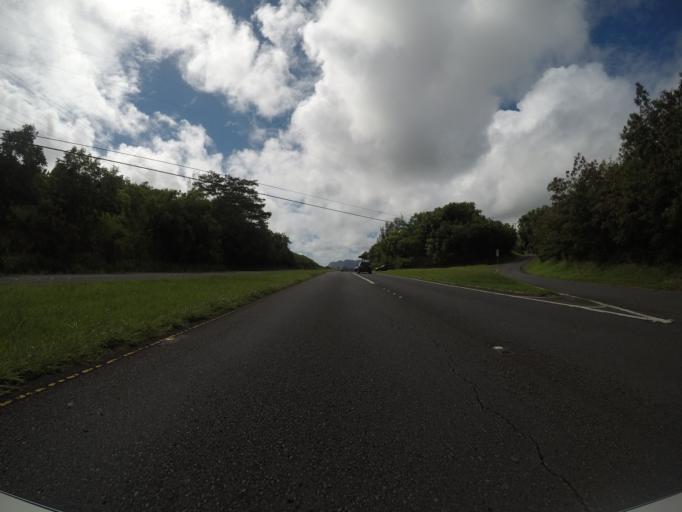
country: US
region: Hawaii
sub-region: Honolulu County
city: Maunawili
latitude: 21.3742
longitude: -157.7456
